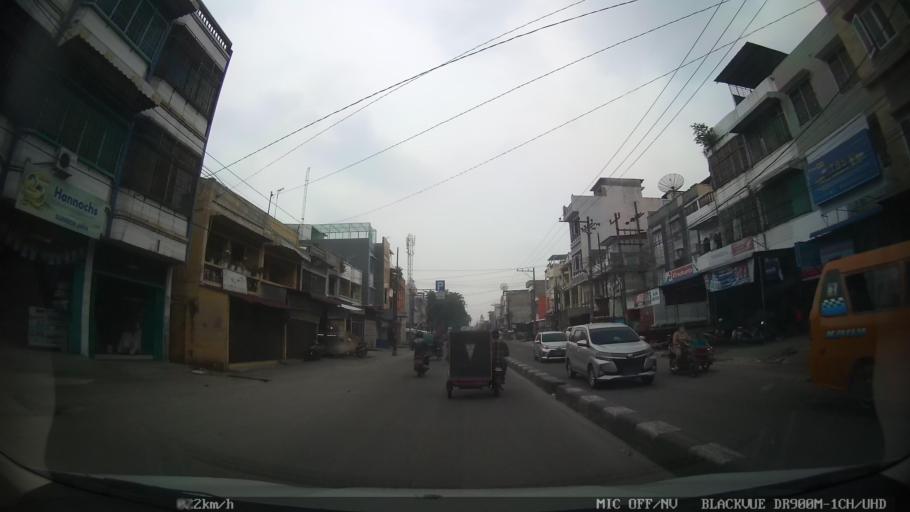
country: ID
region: North Sumatra
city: Medan
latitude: 3.5821
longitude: 98.7060
